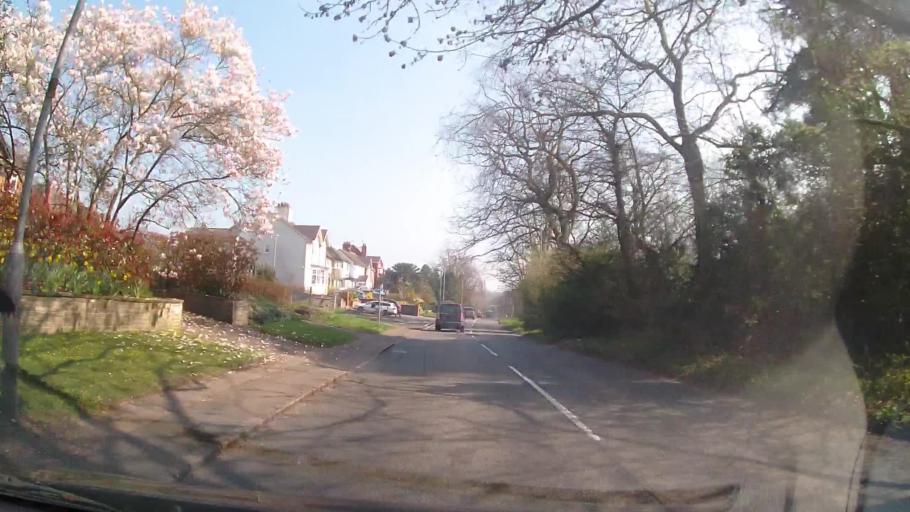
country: GB
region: England
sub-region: Leicestershire
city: Anstey
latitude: 52.6750
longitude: -1.1994
